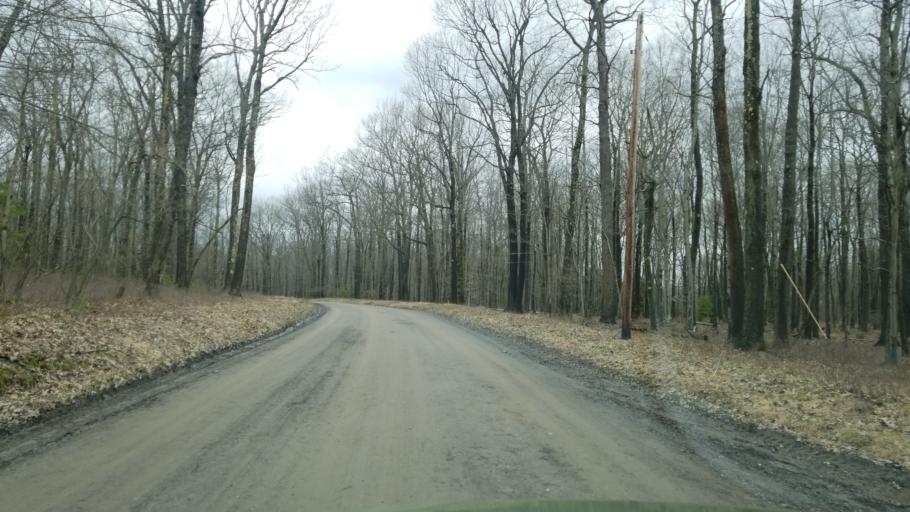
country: US
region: Pennsylvania
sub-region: Clearfield County
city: Shiloh
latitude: 41.1616
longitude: -78.3342
